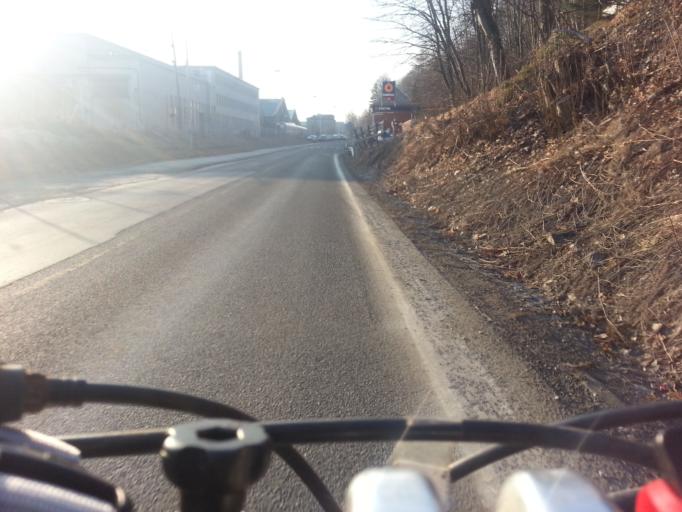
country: NO
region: Sor-Trondelag
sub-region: Trondheim
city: Trondheim
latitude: 63.4221
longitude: 10.3753
